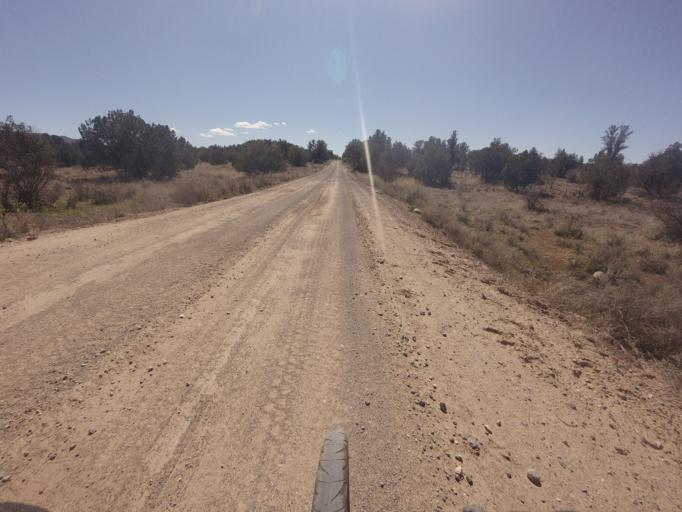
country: US
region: Arizona
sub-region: Yavapai County
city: Lake Montezuma
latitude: 34.6141
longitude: -111.7250
